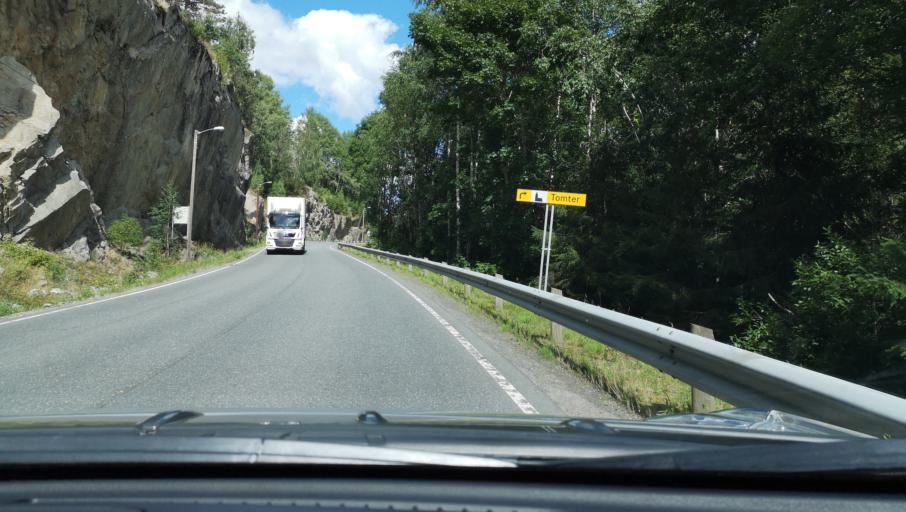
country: NO
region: Ostfold
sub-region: Hobol
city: Tomter
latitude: 59.6537
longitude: 10.9995
